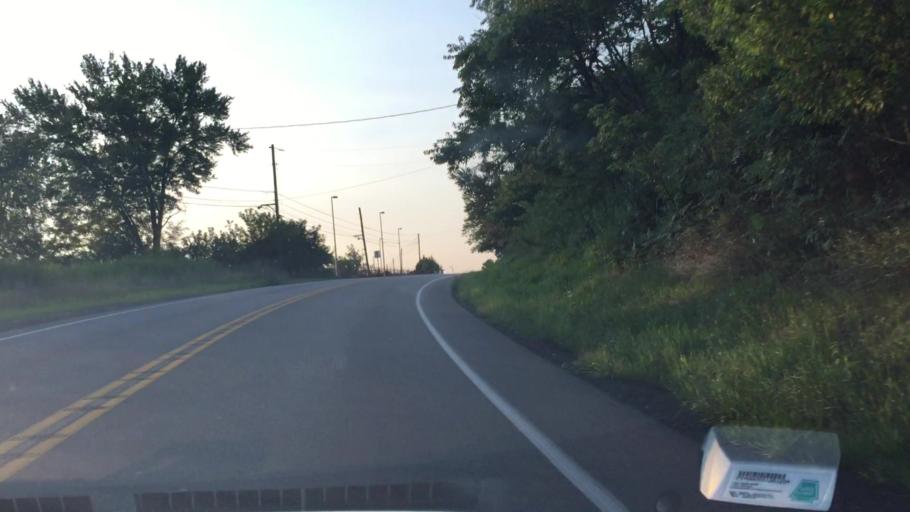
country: US
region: Pennsylvania
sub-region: Butler County
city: Evans City
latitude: 40.7436
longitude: -80.0337
